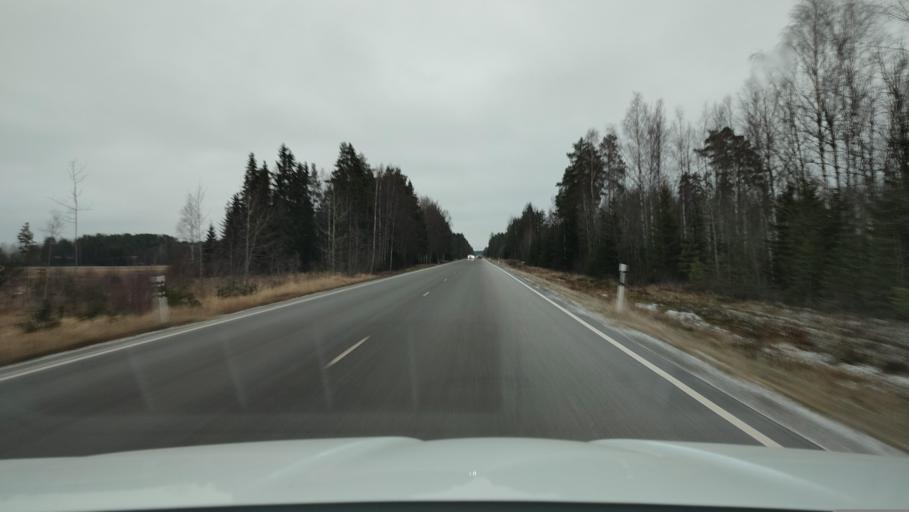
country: FI
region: Ostrobothnia
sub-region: Sydosterbotten
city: Naerpes
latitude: 62.5260
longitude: 21.4602
